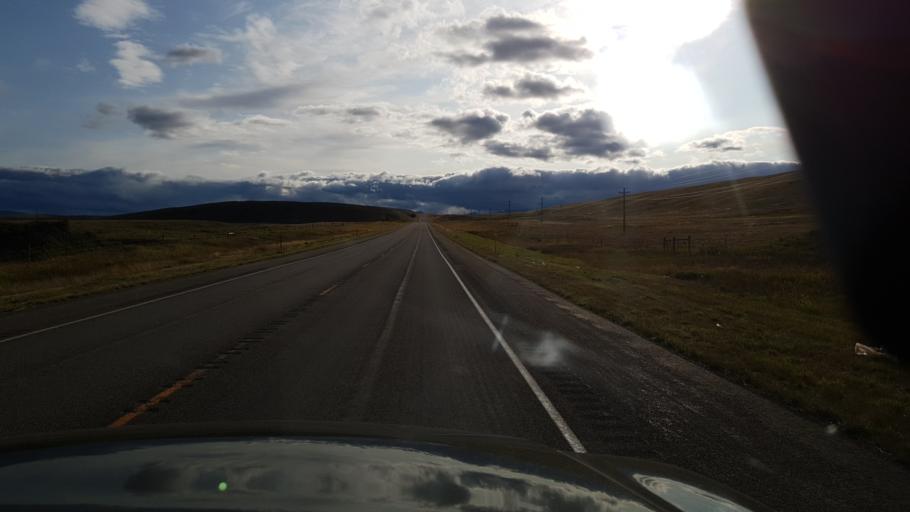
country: US
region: Montana
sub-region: Glacier County
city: South Browning
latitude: 48.5259
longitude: -113.0644
